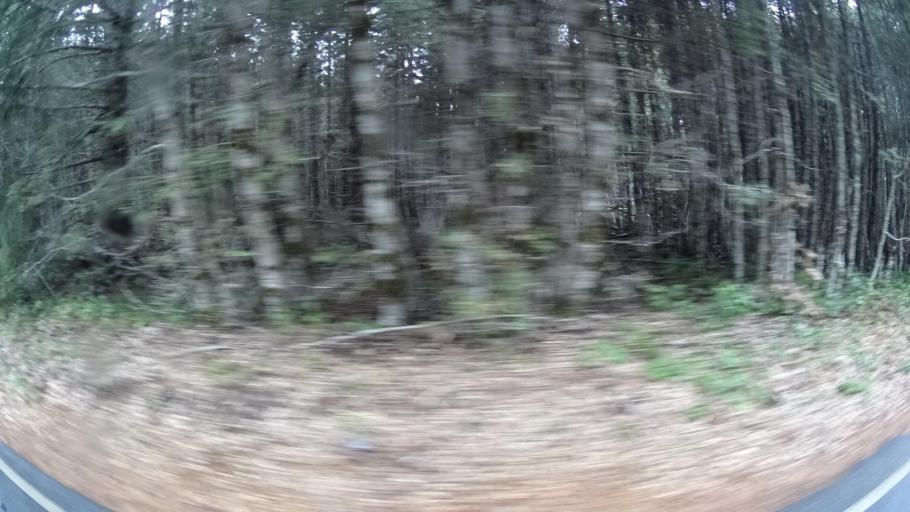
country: US
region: California
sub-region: Humboldt County
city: Willow Creek
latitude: 41.1907
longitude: -123.8143
